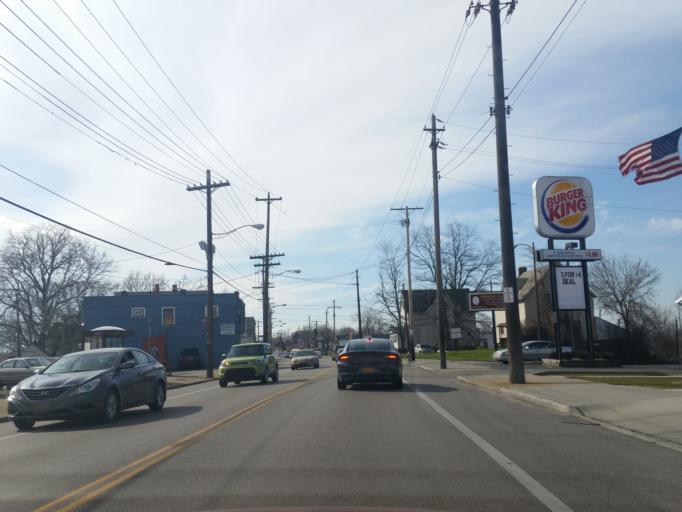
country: US
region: Ohio
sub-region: Cuyahoga County
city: Brooklyn
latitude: 41.4608
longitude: -81.7340
